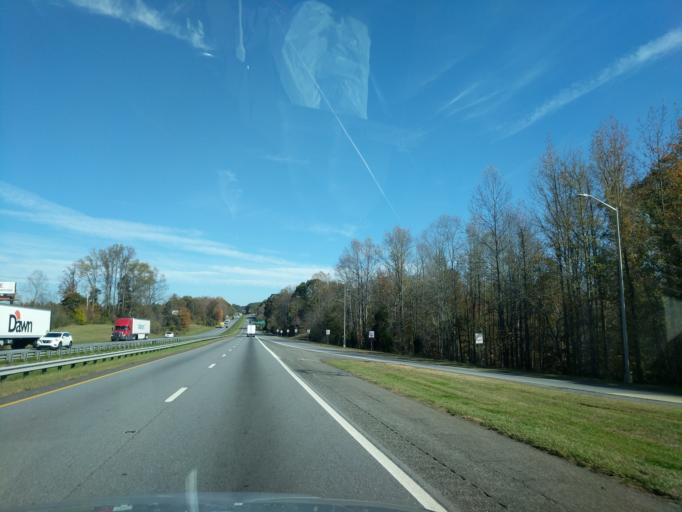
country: US
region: North Carolina
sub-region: Cleveland County
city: White Plains
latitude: 35.1855
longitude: -81.4059
